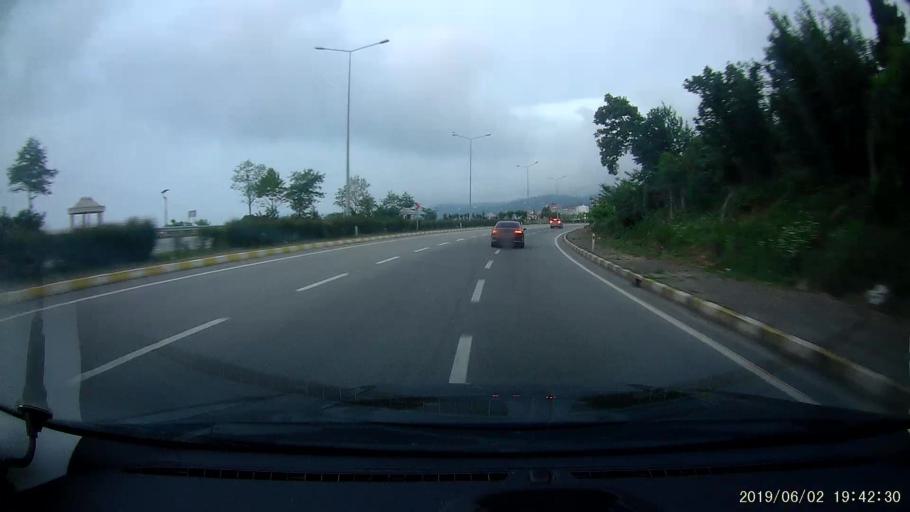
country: TR
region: Giresun
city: Kesap
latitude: 40.9176
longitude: 38.5063
